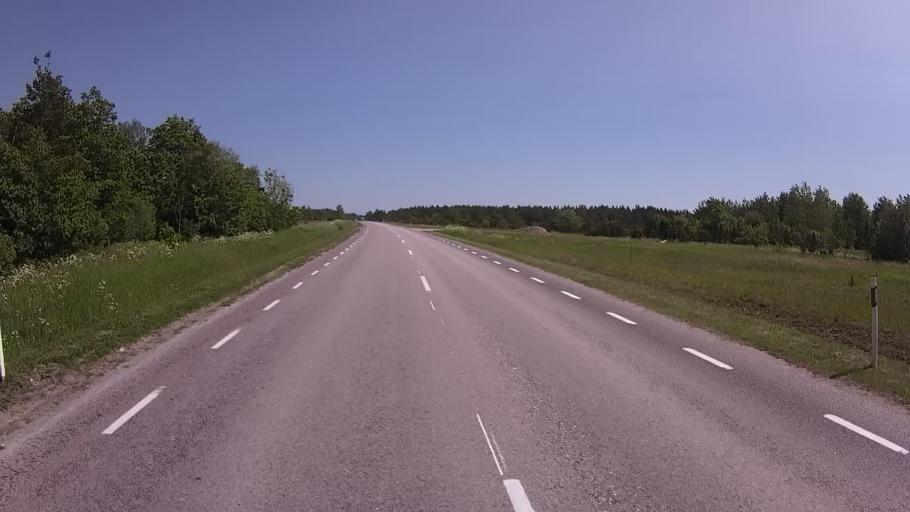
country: EE
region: Saare
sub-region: Kuressaare linn
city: Kuressaare
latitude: 58.2885
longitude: 22.3951
